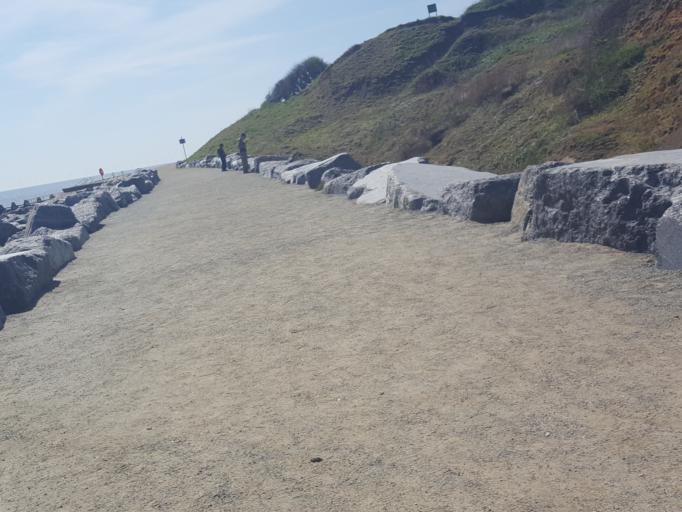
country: GB
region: England
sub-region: Essex
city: Walton-on-the-Naze
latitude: 51.8643
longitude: 1.2898
